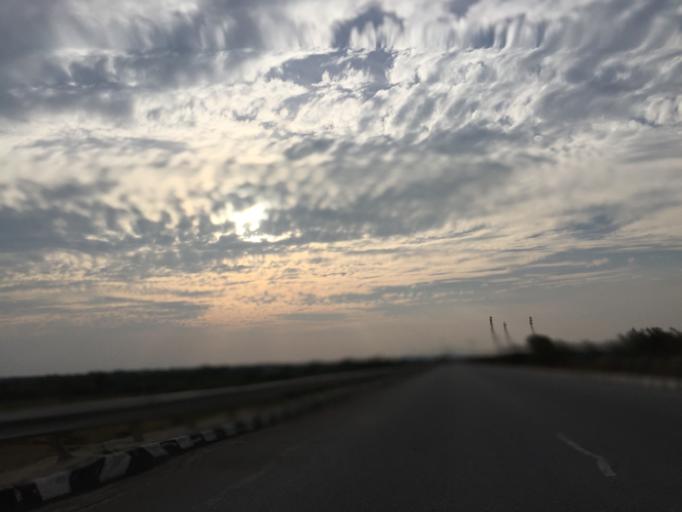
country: IN
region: Karnataka
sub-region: Kolar
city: Mulbagal
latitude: 13.1468
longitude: 78.2650
